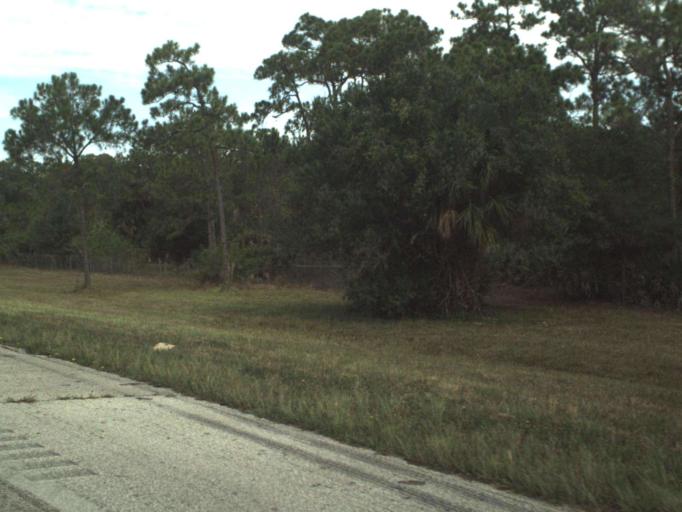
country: US
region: Florida
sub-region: Martin County
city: Palm City
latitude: 27.1274
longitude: -80.3209
